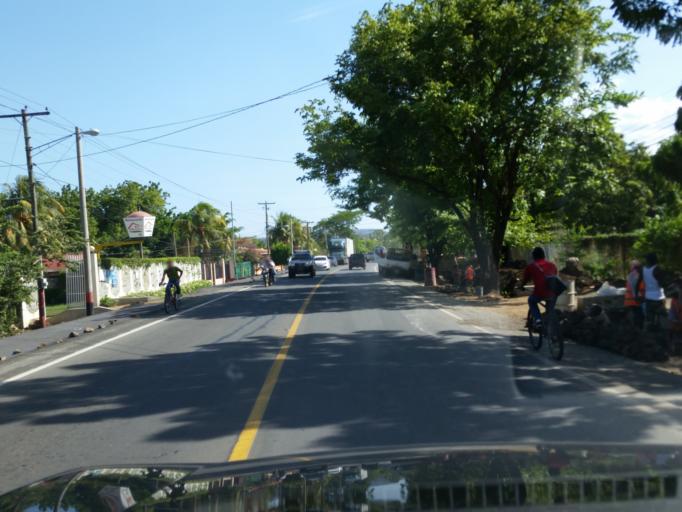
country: NI
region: Leon
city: Leon
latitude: 12.4251
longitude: -86.8664
